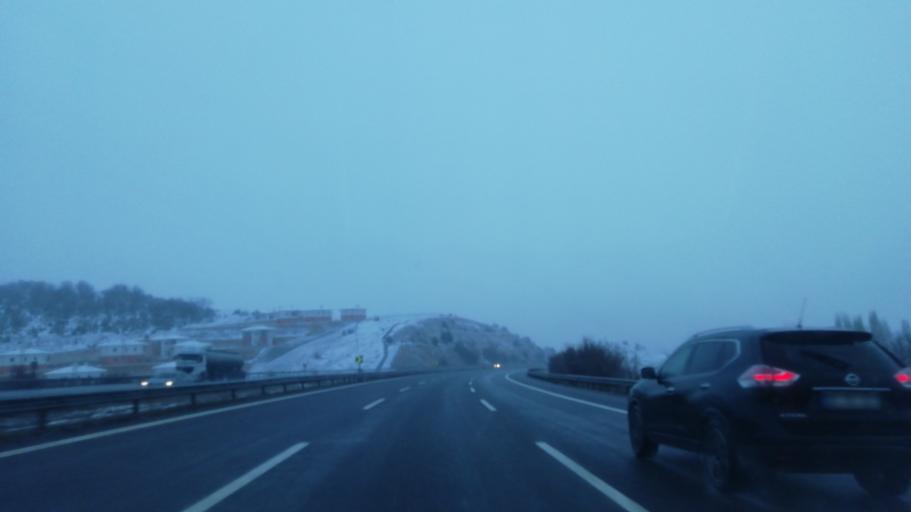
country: TR
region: Bolu
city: Bolu
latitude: 40.7403
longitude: 31.5420
